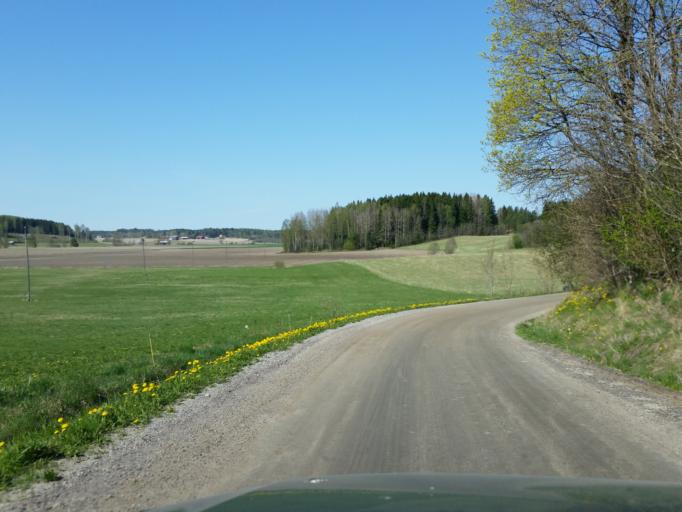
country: FI
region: Uusimaa
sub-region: Helsinki
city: Karjalohja
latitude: 60.1408
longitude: 23.7387
